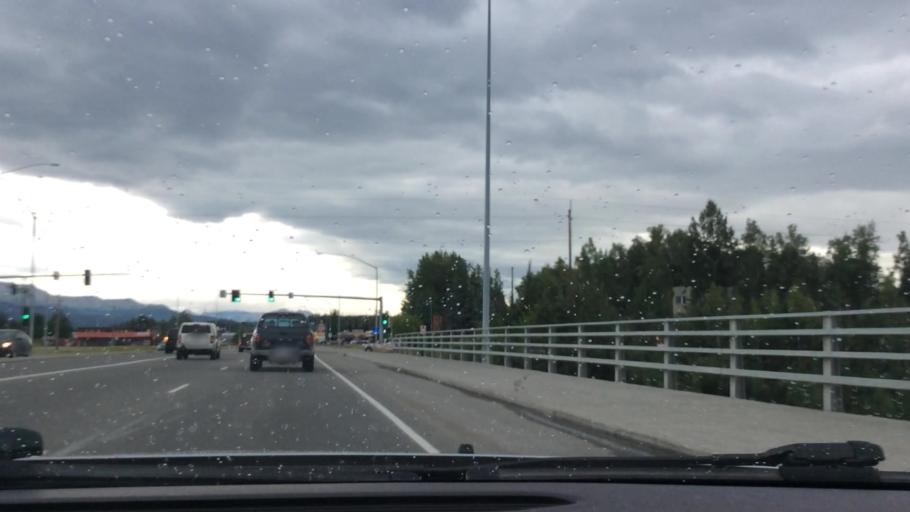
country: US
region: Alaska
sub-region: Anchorage Municipality
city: Anchorage
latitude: 61.2251
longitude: -149.7788
